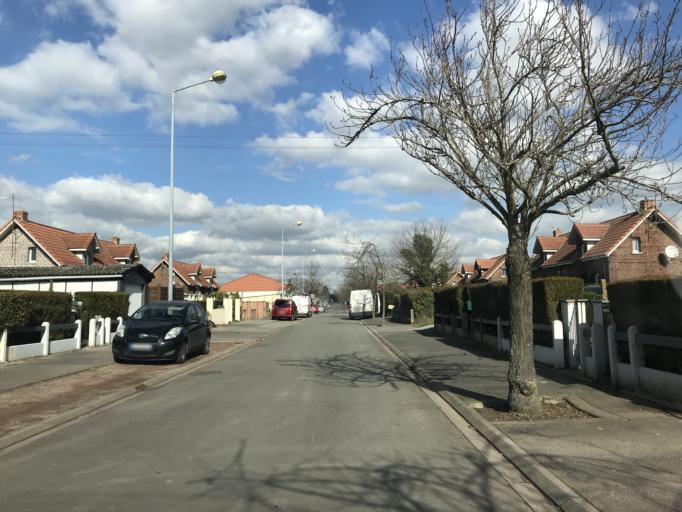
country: FR
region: Nord-Pas-de-Calais
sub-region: Departement du Pas-de-Calais
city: Bully-les-Mines
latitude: 50.4548
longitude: 2.7220
